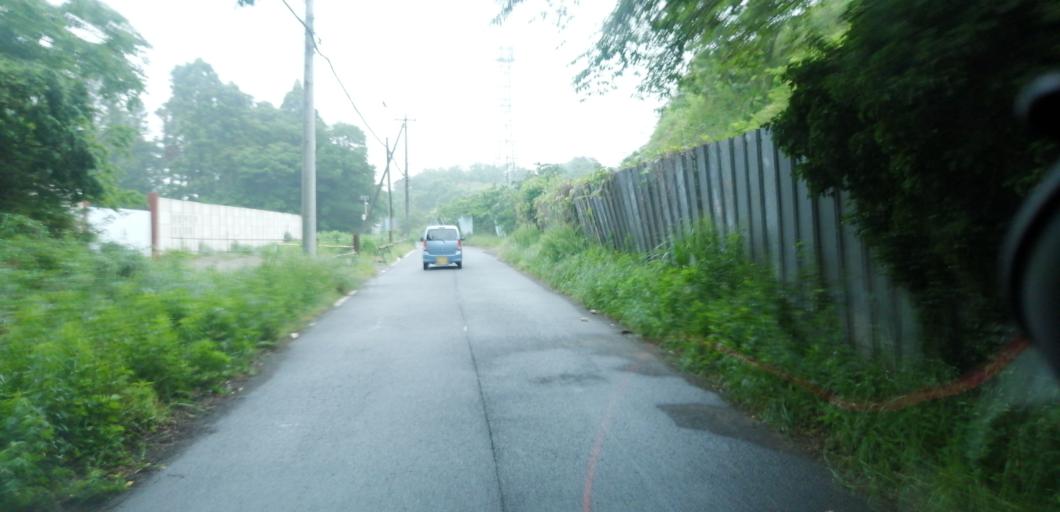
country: JP
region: Chiba
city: Ichihara
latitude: 35.4760
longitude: 140.1499
